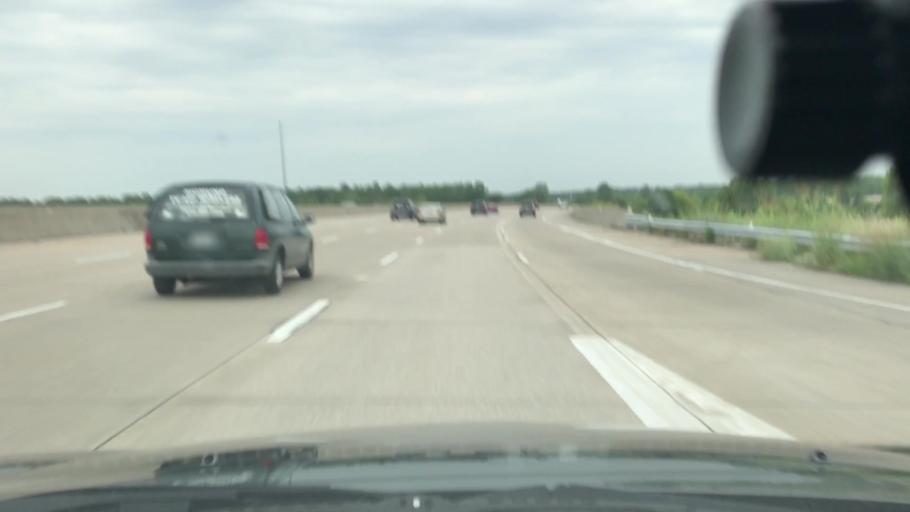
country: US
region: Missouri
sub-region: Saint Louis County
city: Maryland Heights
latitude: 38.7075
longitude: -90.5011
